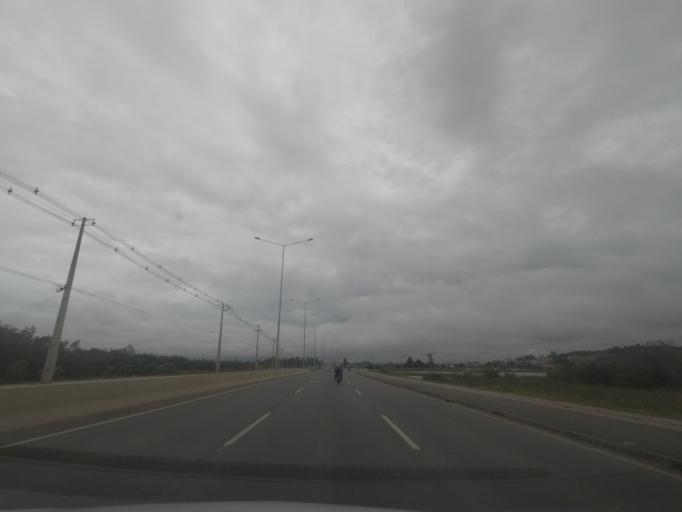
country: BR
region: Parana
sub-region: Pinhais
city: Pinhais
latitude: -25.4439
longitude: -49.1444
